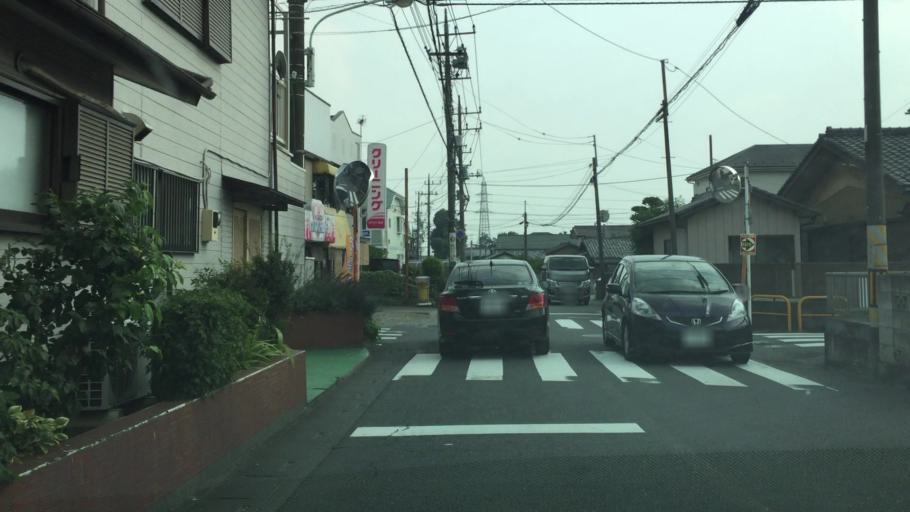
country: JP
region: Saitama
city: Yono
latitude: 35.9136
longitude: 139.6054
